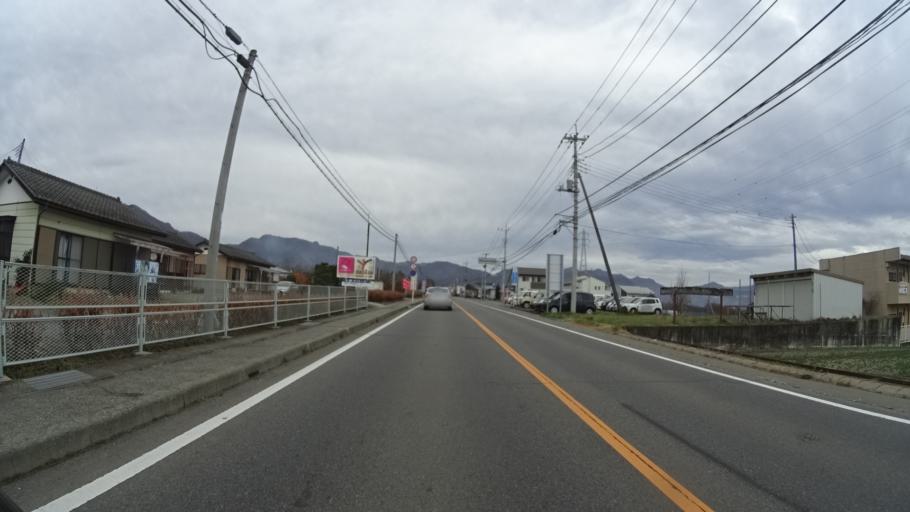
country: JP
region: Gunma
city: Numata
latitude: 36.6634
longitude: 139.1280
